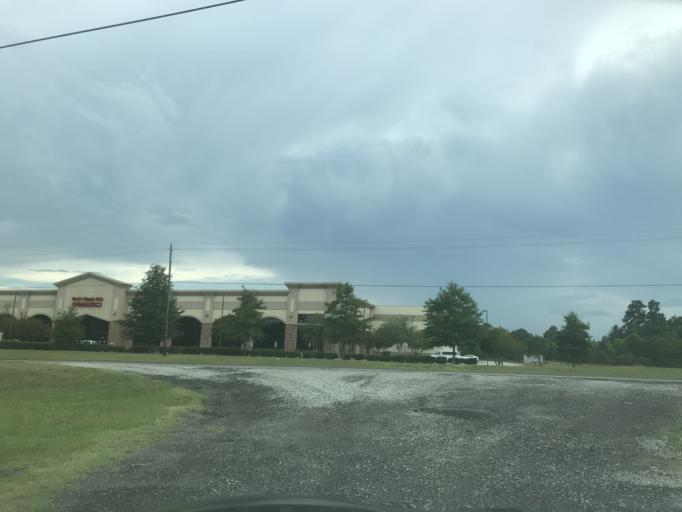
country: US
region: North Carolina
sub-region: Johnston County
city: Clayton
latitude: 35.6315
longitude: -78.4339
